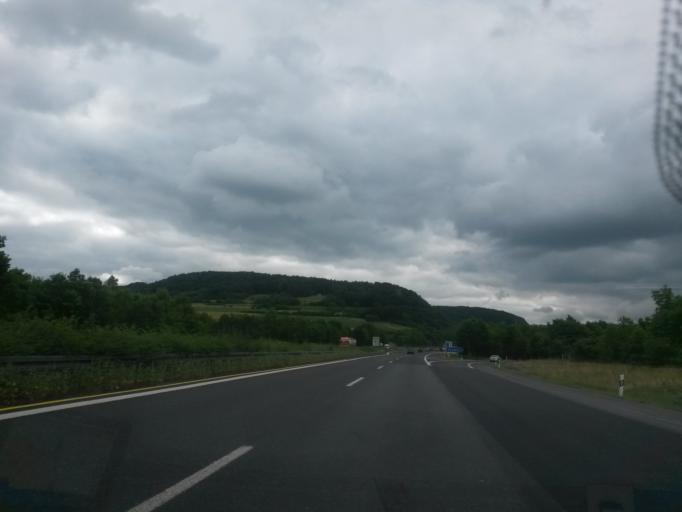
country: DE
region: Bavaria
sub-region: Regierungsbezirk Unterfranken
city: Elfershausen
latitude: 50.1276
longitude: 9.9574
